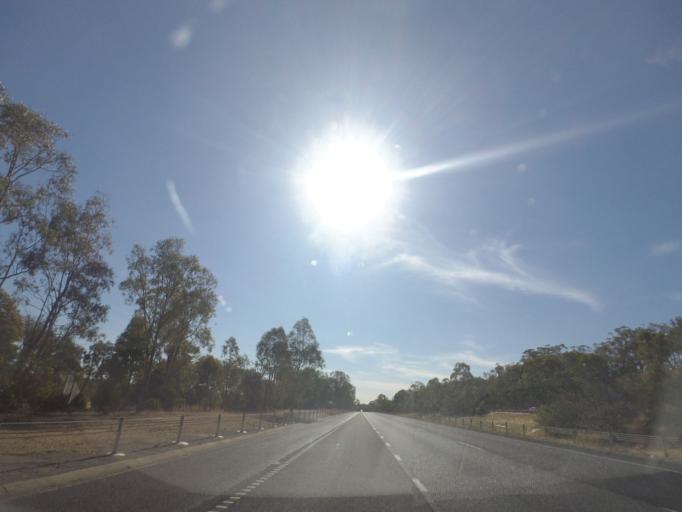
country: AU
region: Victoria
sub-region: Murrindindi
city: Kinglake West
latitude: -36.9837
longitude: 145.1358
